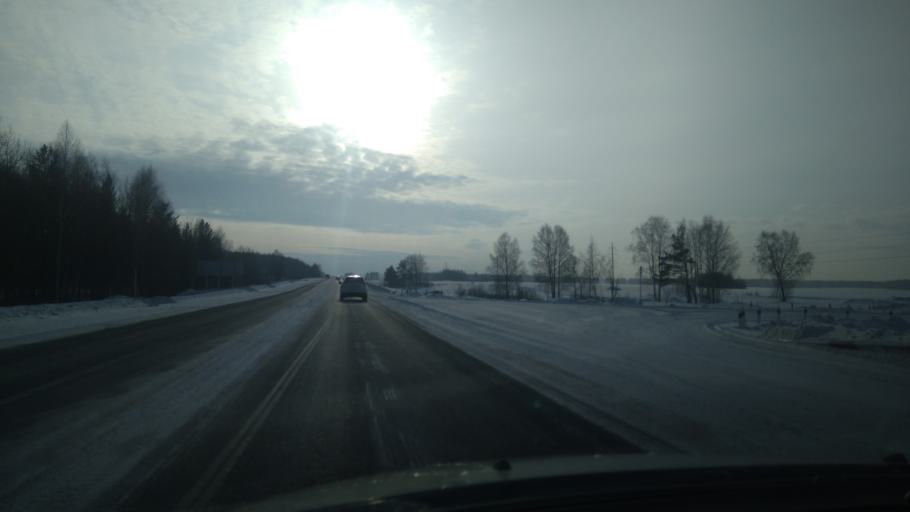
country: RU
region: Sverdlovsk
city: Bogdanovich
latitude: 56.8442
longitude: 62.0503
